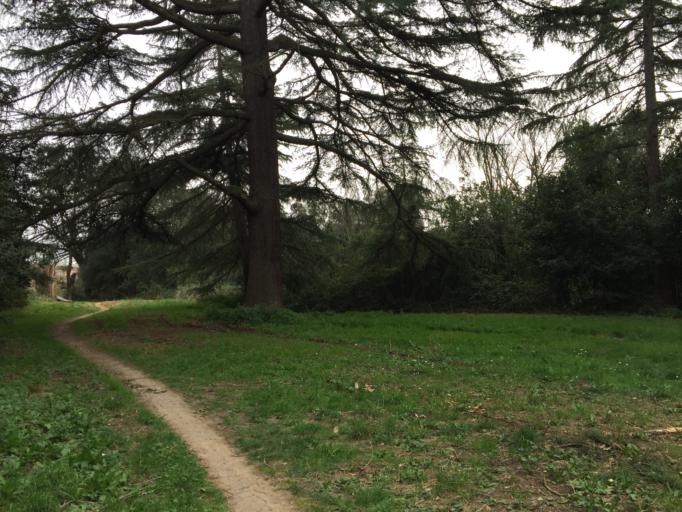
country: VA
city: Vatican City
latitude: 41.8823
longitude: 12.4476
